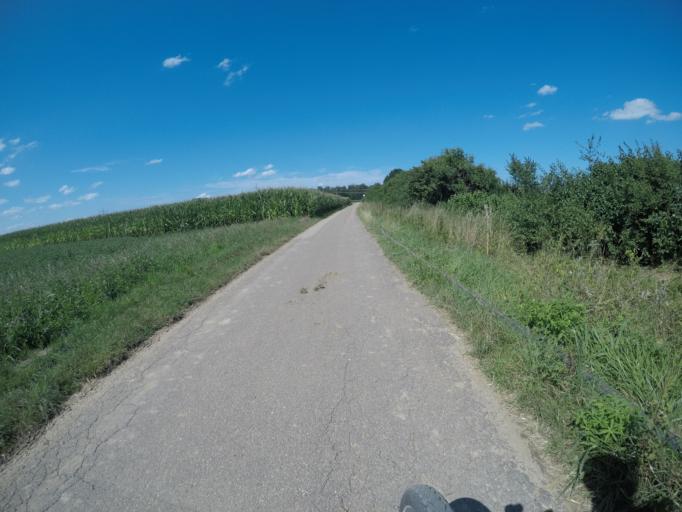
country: DE
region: Baden-Wuerttemberg
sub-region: Regierungsbezirk Stuttgart
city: Ostfildern
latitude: 48.7019
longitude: 9.2385
